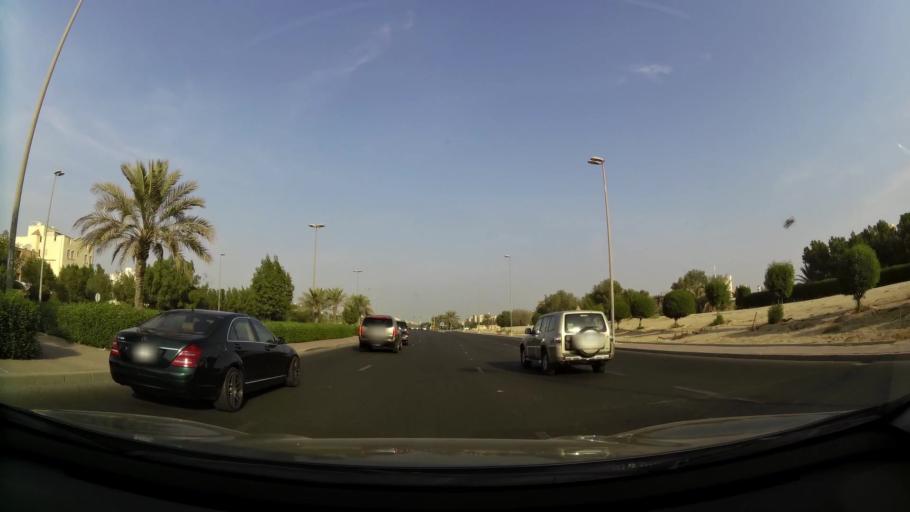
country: KW
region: Mubarak al Kabir
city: Mubarak al Kabir
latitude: 29.2077
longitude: 48.0667
